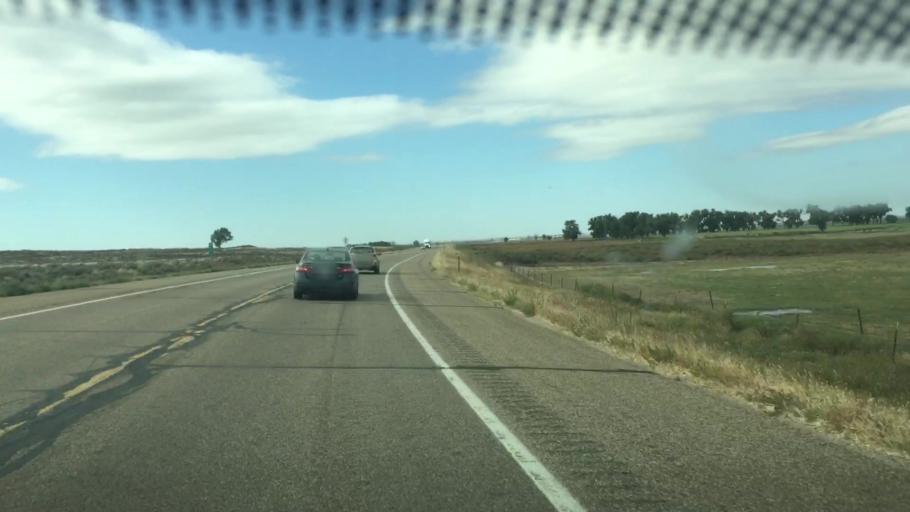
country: US
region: Colorado
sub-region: Prowers County
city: Lamar
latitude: 38.0646
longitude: -102.3605
